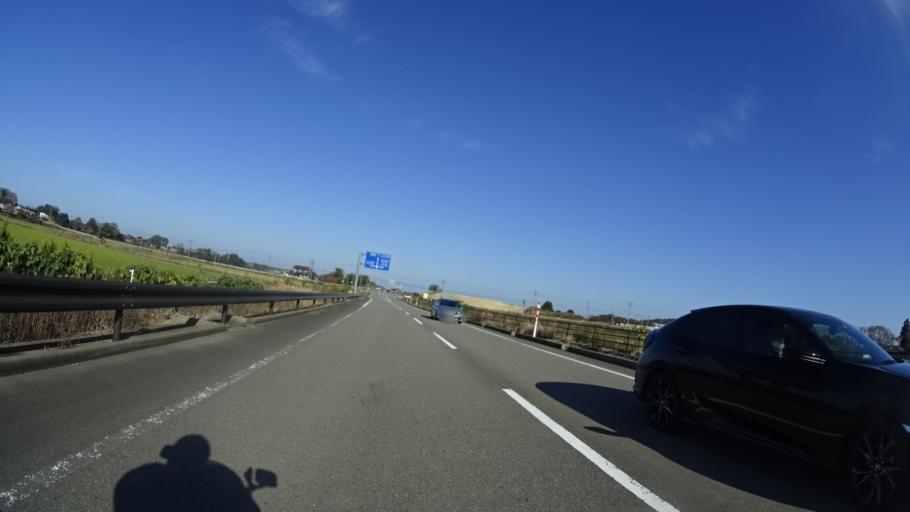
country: JP
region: Ishikawa
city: Komatsu
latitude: 36.2996
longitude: 136.3877
